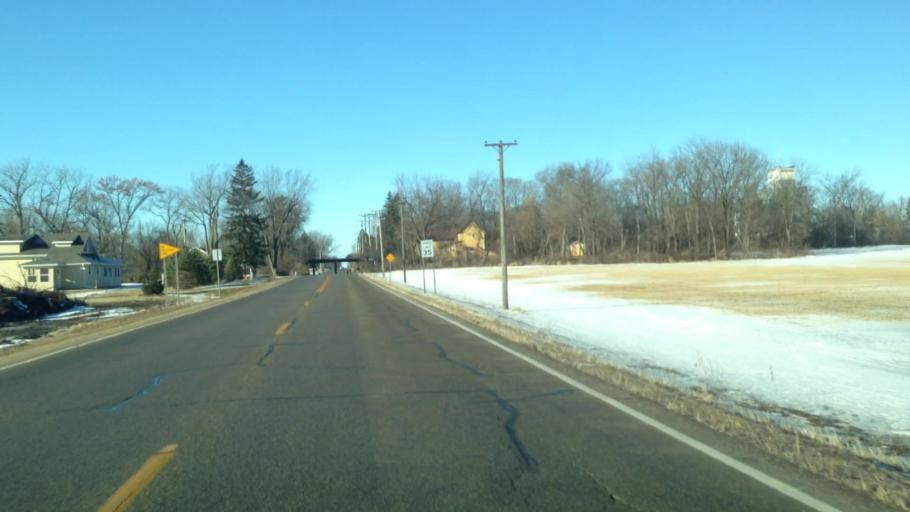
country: US
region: Minnesota
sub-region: Rice County
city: Northfield
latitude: 44.5437
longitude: -93.1487
